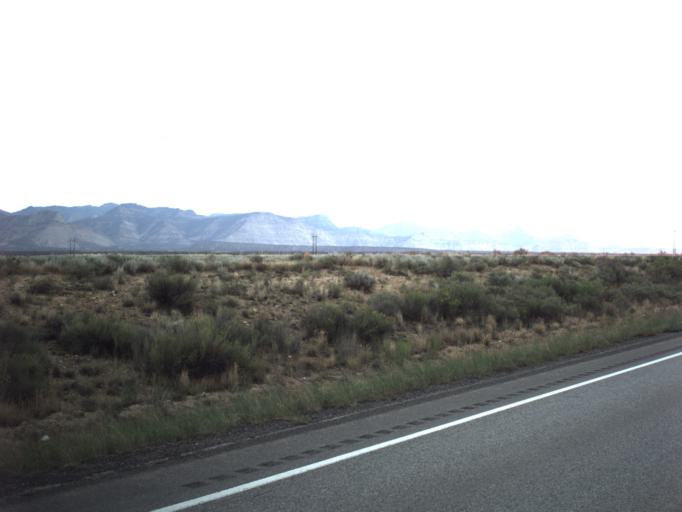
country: US
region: Utah
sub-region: Carbon County
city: East Carbon City
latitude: 39.4498
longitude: -110.4744
